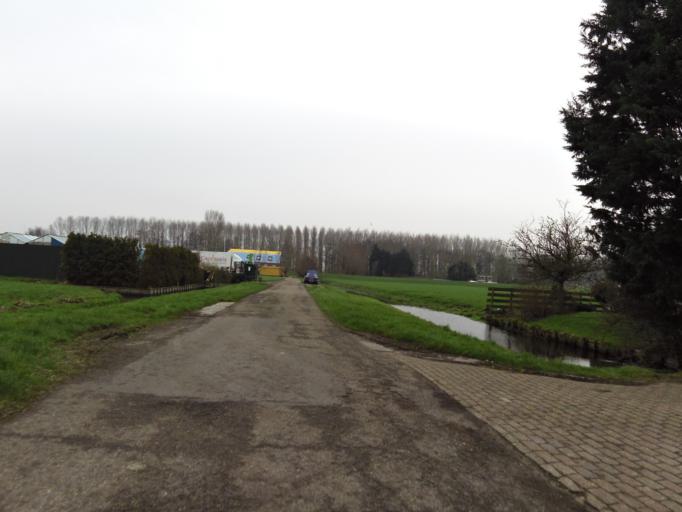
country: NL
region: South Holland
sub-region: Gemeente Leiderdorp
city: Leiderdorp
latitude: 52.1697
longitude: 4.5583
